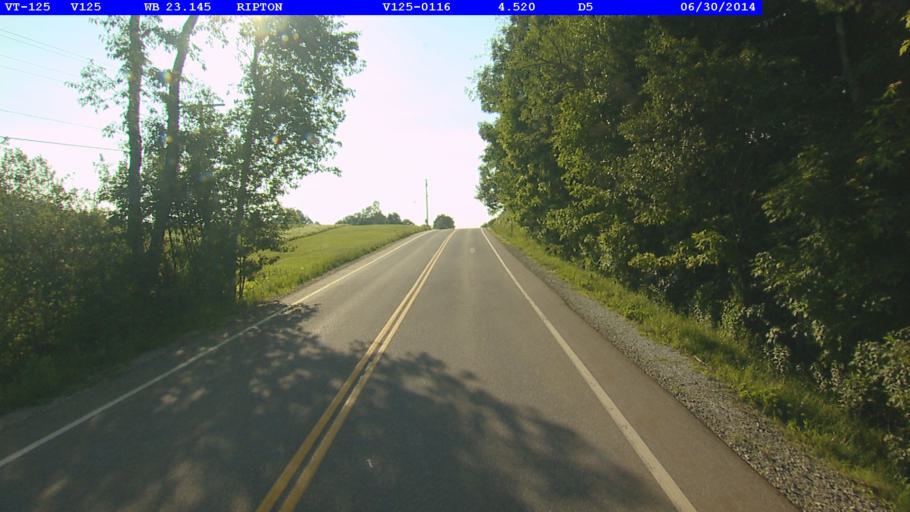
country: US
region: Vermont
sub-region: Rutland County
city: Brandon
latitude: 43.9515
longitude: -72.9884
